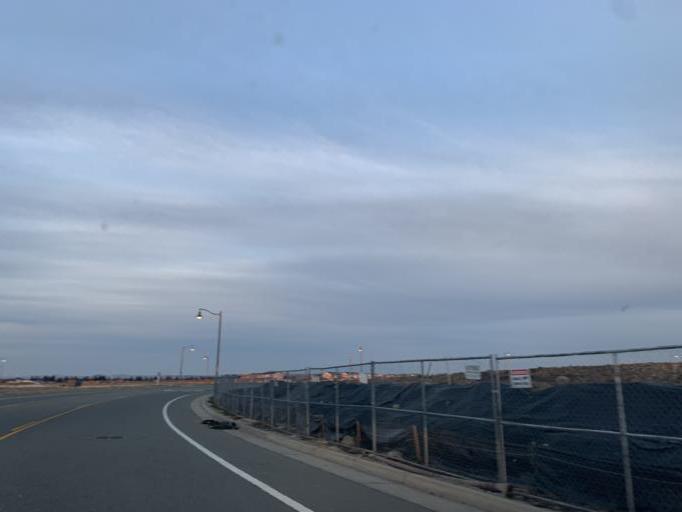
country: US
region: California
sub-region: Placer County
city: Lincoln
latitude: 38.8556
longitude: -121.2945
